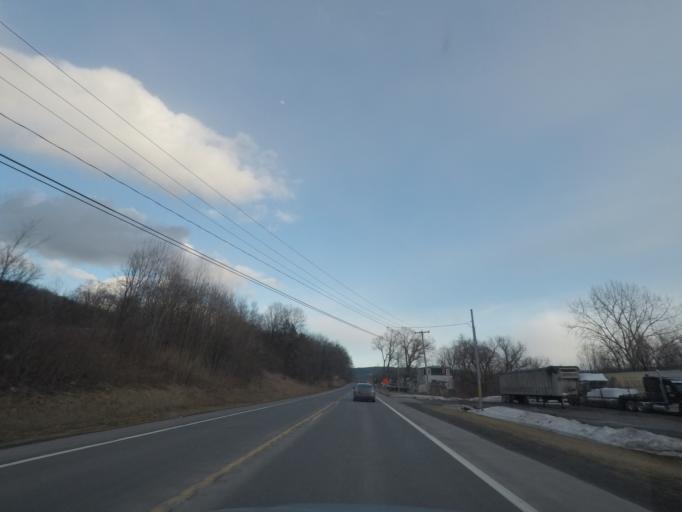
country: US
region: New York
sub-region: Herkimer County
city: Ilion
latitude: 43.0257
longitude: -75.0381
